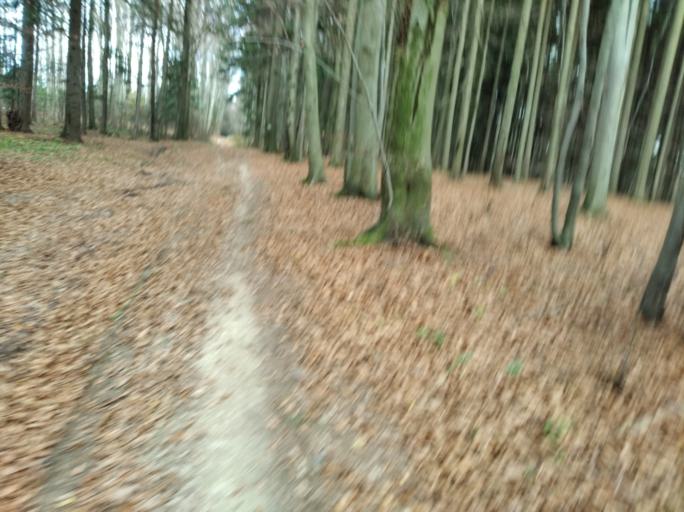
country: PL
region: Subcarpathian Voivodeship
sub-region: Powiat strzyzowski
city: Jawornik
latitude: 49.8607
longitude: 21.8544
